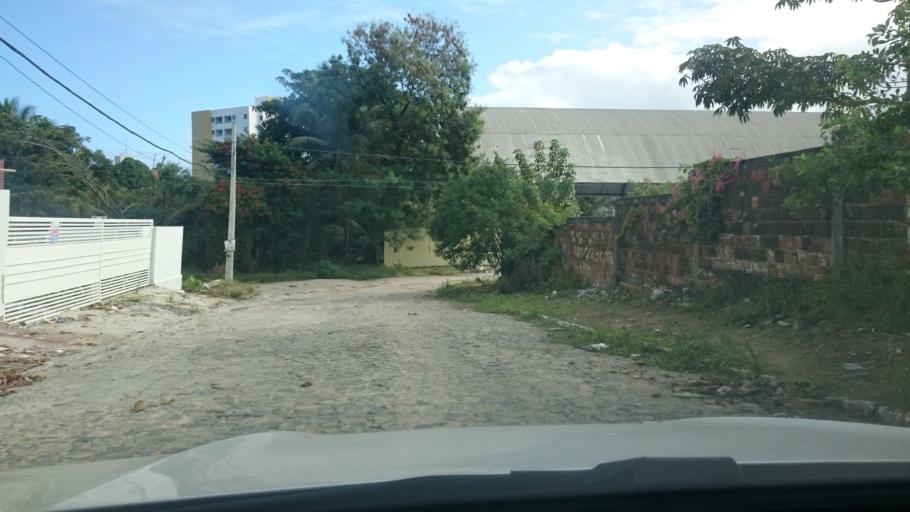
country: BR
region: Paraiba
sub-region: Joao Pessoa
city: Joao Pessoa
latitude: -7.1505
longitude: -34.8444
